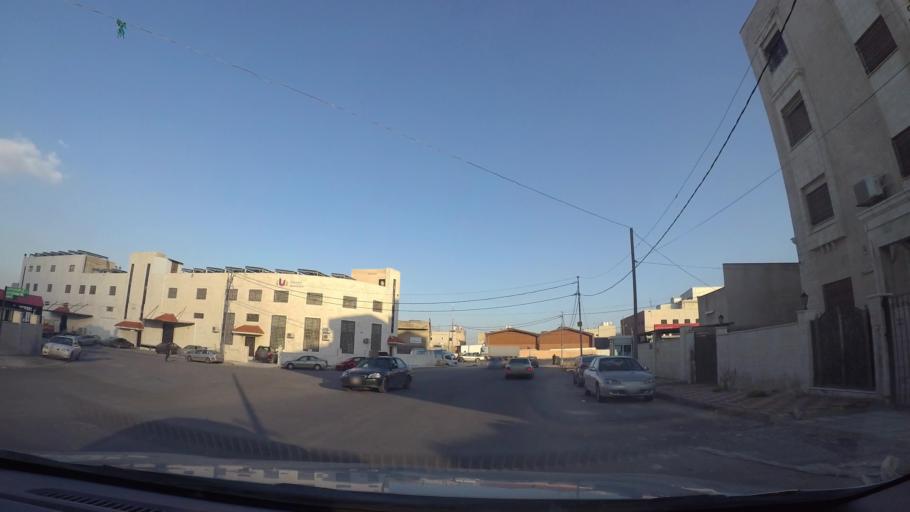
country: JO
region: Amman
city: Al Bunayyat ash Shamaliyah
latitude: 31.9083
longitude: 35.9178
